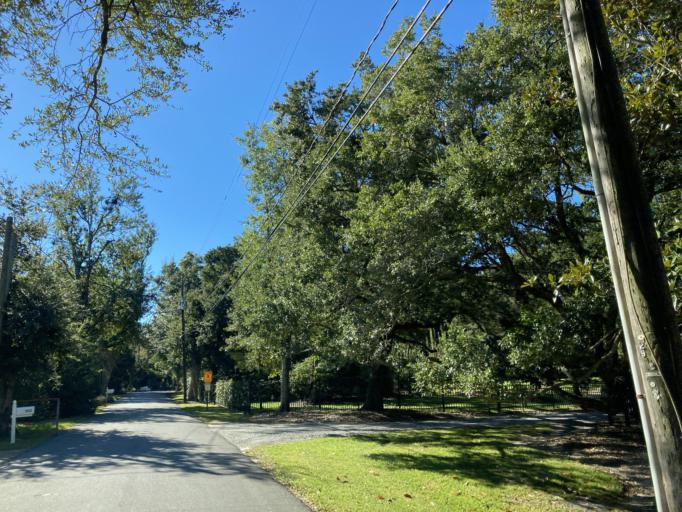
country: US
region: Mississippi
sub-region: Jackson County
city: Gulf Hills
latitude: 30.4191
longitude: -88.8429
